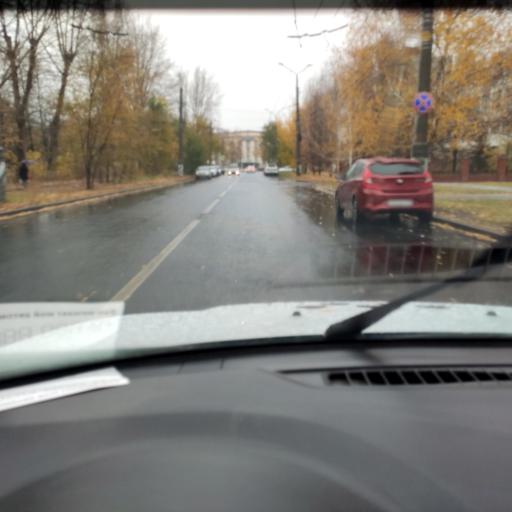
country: RU
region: Samara
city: Tol'yatti
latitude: 53.5168
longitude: 49.4565
